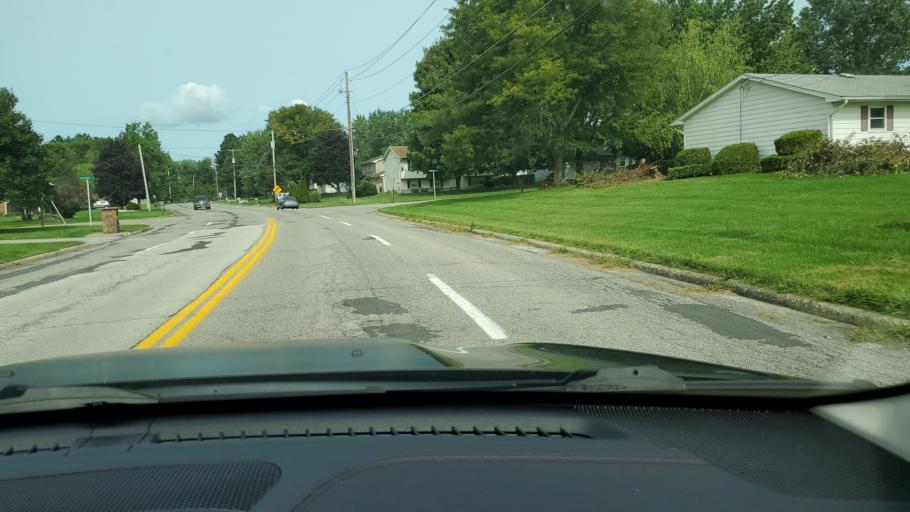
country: US
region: Ohio
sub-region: Mahoning County
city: Boardman
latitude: 40.9899
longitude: -80.6696
